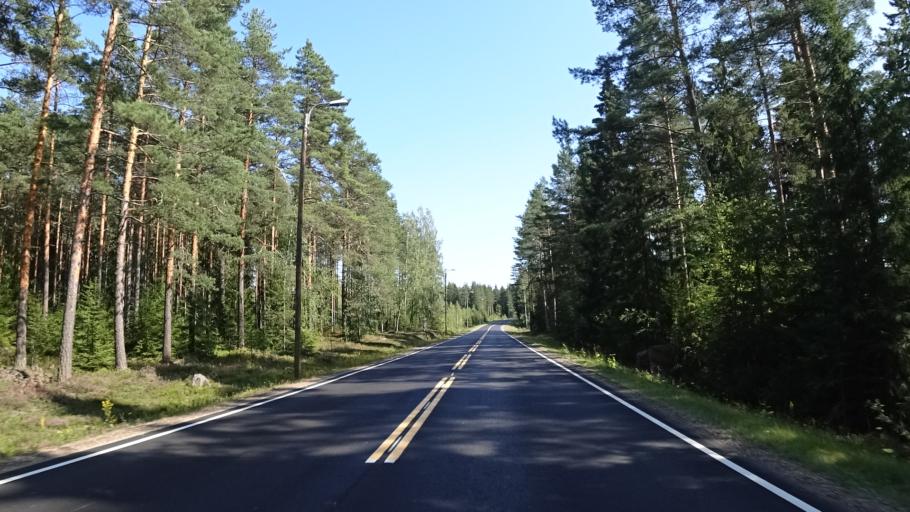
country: FI
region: Kymenlaakso
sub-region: Kotka-Hamina
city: Karhula
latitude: 60.5535
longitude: 26.9021
